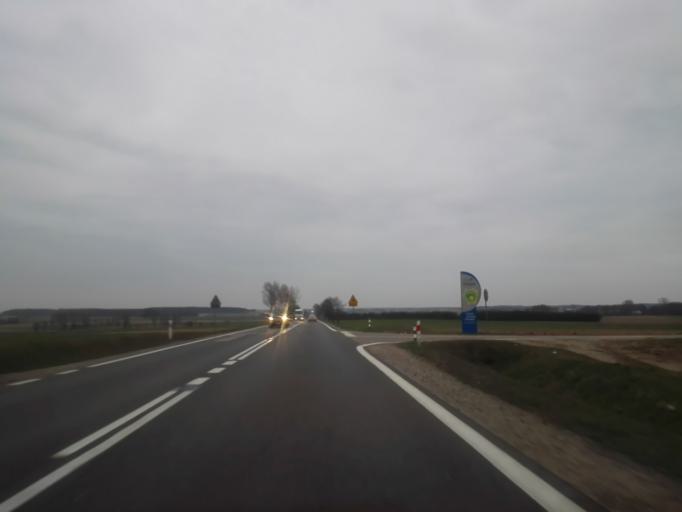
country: PL
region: Podlasie
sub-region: Powiat kolnenski
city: Stawiski
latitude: 53.4320
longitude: 22.1718
